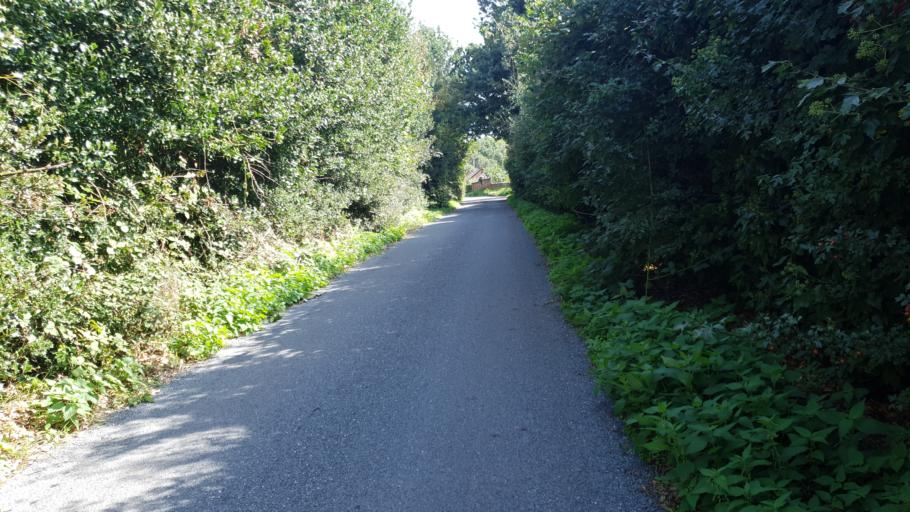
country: GB
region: England
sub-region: Essex
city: Colchester
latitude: 51.9244
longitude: 0.9401
